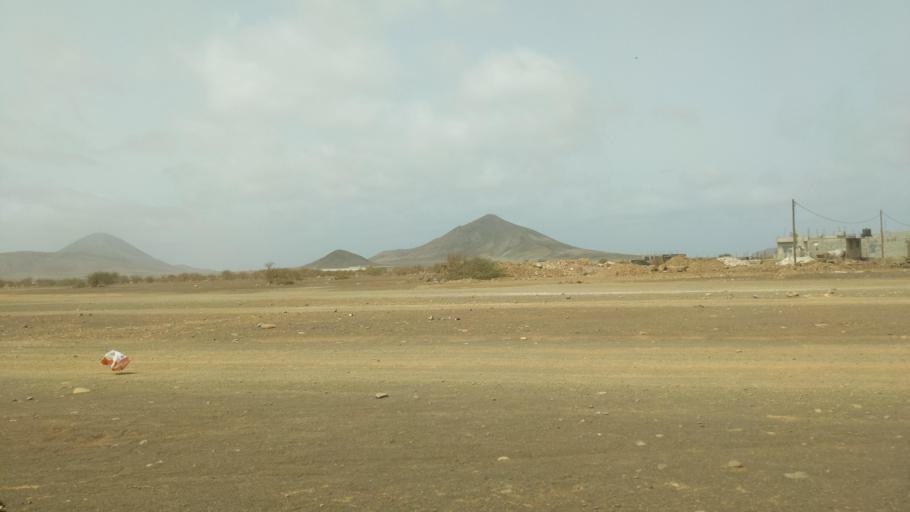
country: CV
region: Sal
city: Espargos
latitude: 16.7680
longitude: -22.9452
